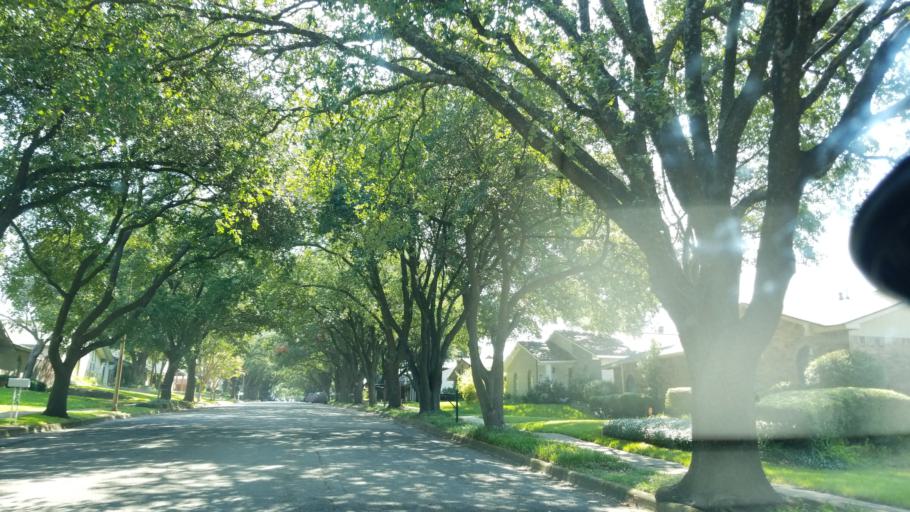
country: US
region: Texas
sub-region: Dallas County
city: Garland
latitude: 32.8768
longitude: -96.6979
